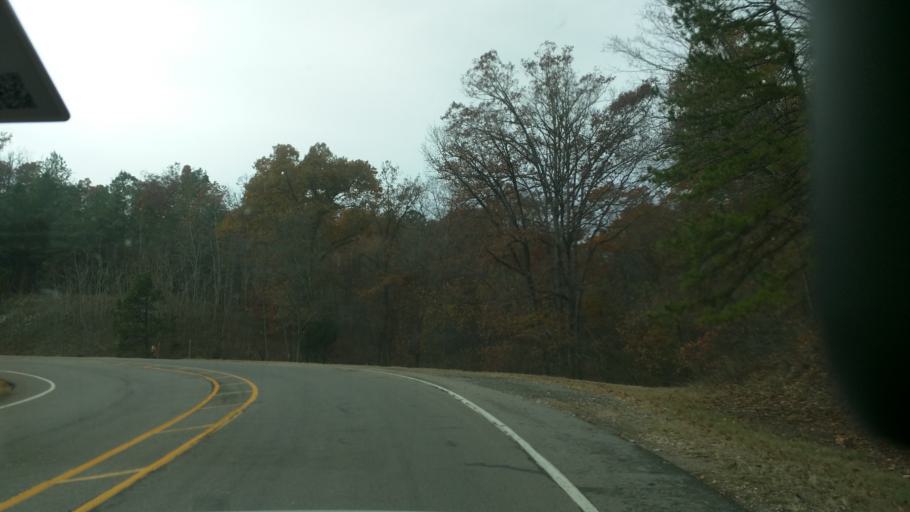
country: US
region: Oklahoma
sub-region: Cherokee County
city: Tahlequah
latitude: 35.9291
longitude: -94.8439
